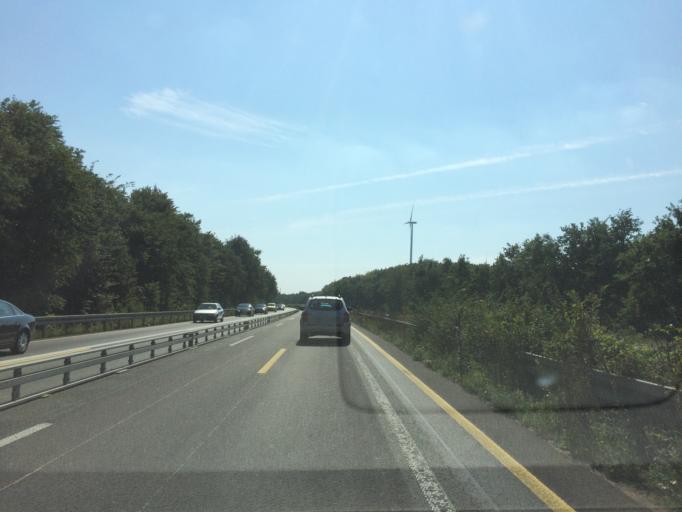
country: DE
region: North Rhine-Westphalia
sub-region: Regierungsbezirk Munster
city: Haltern
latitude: 51.6954
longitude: 7.1479
